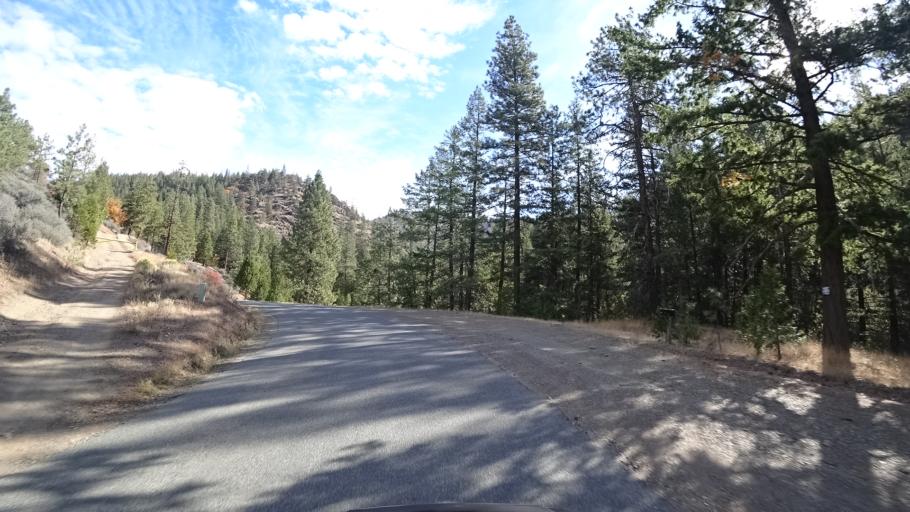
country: US
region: California
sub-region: Siskiyou County
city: Yreka
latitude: 41.6304
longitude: -122.7204
